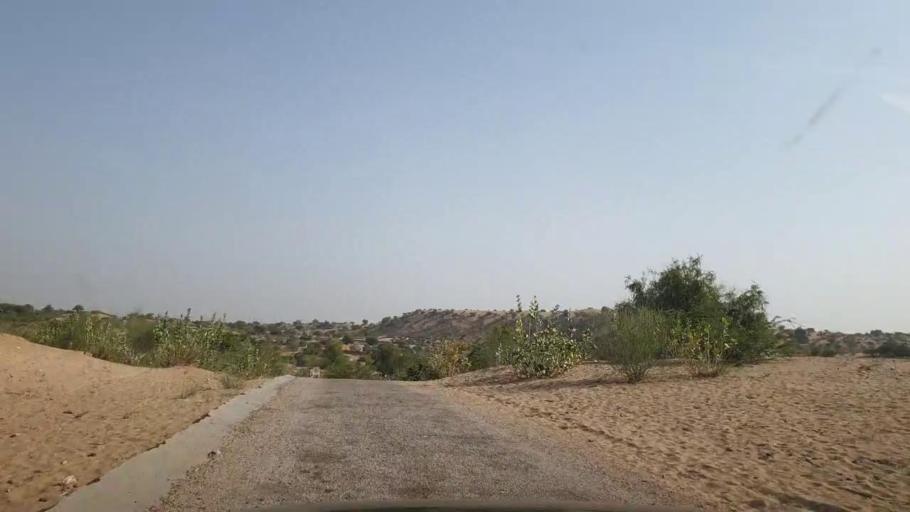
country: PK
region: Sindh
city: Islamkot
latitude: 25.1261
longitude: 70.5053
